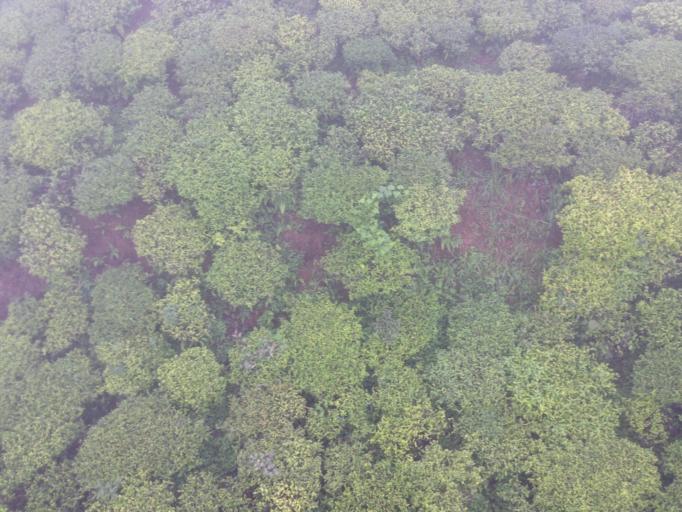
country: IN
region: West Bengal
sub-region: Darjiling
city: Darjiling
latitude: 27.0683
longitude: 88.2545
